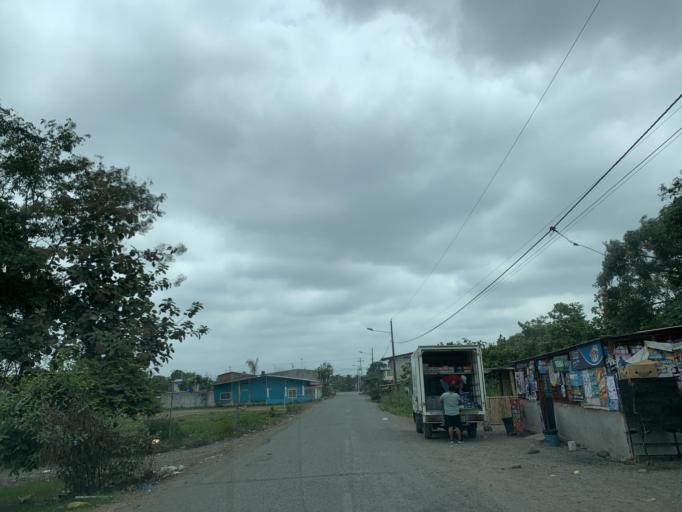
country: EC
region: Guayas
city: Coronel Marcelino Mariduena
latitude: -2.3181
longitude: -79.4699
